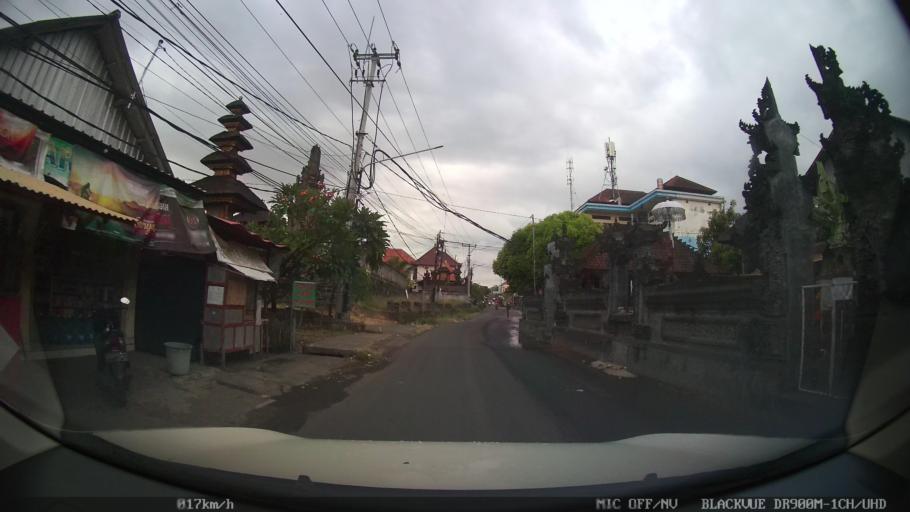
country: ID
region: Bali
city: Banjar Kertajiwa
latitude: -8.6397
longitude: 115.2698
